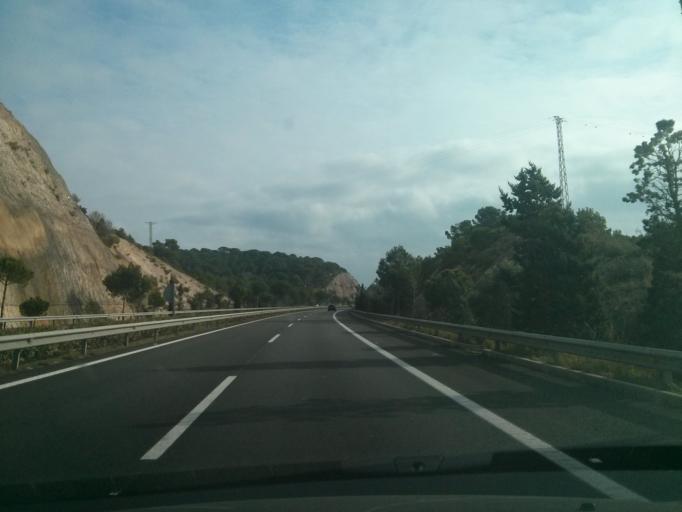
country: ES
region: Catalonia
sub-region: Provincia de Tarragona
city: Cunit
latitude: 41.2136
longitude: 1.6355
